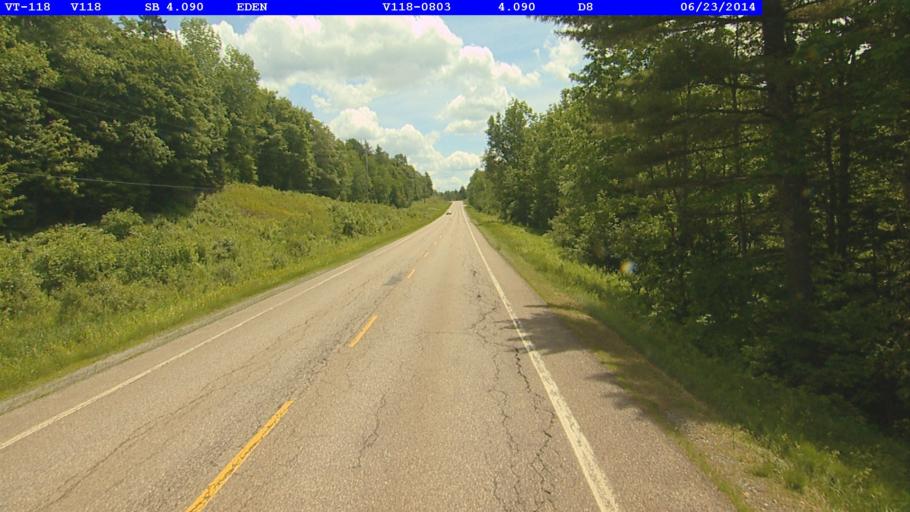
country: US
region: Vermont
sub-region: Lamoille County
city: Johnson
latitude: 44.7577
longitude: -72.5822
